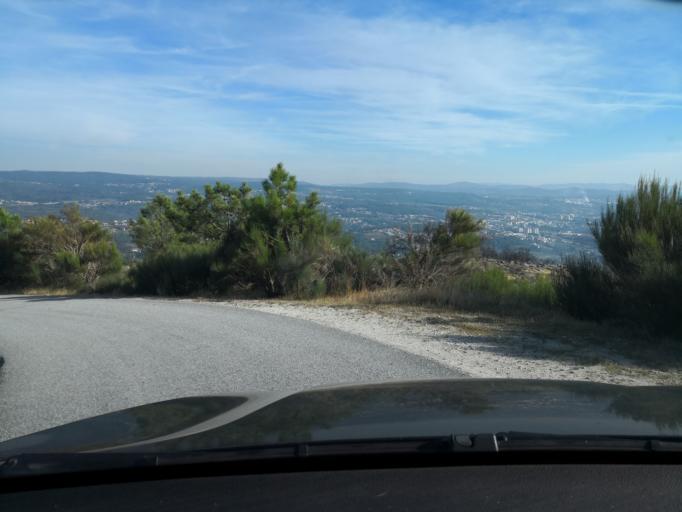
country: PT
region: Vila Real
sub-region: Vila Real
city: Vila Real
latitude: 41.3415
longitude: -7.7570
